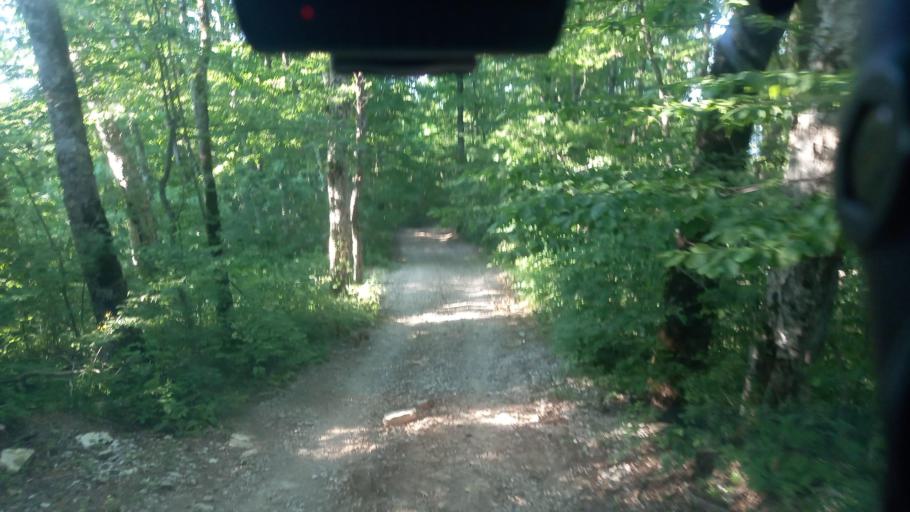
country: RU
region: Krasnodarskiy
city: Gelendzhik
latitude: 44.6242
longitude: 38.1886
